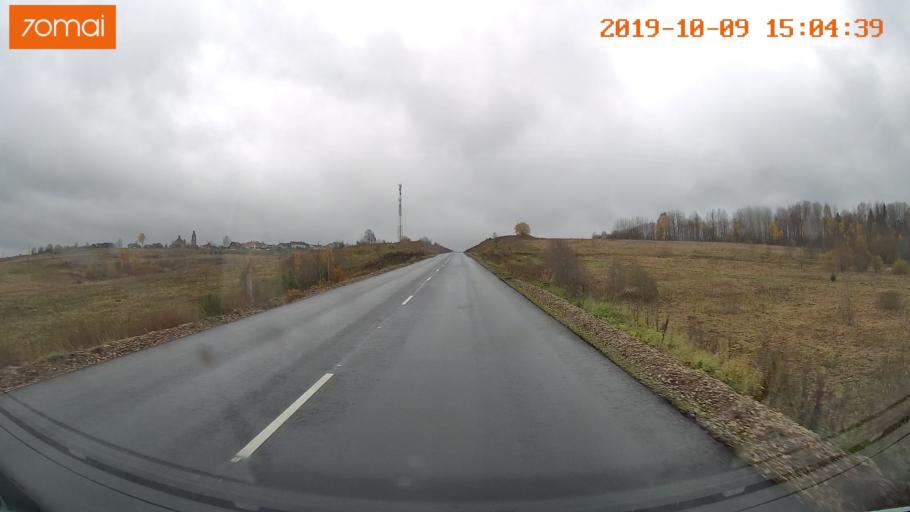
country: RU
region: Kostroma
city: Chistyye Bory
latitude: 58.2562
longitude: 41.6652
